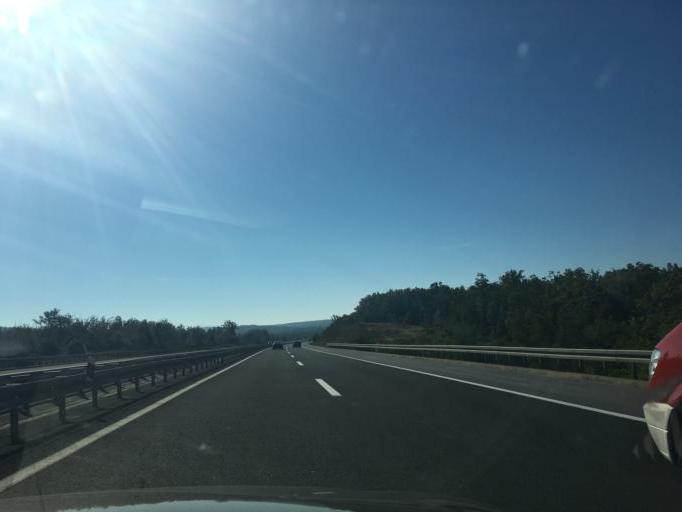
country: HR
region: Licko-Senjska
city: Gospic
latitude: 44.7344
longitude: 15.3812
